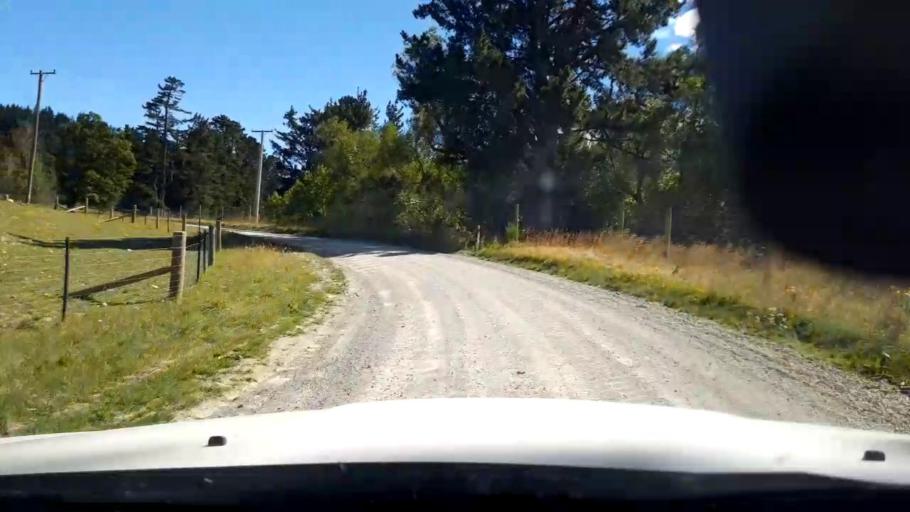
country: NZ
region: Canterbury
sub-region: Timaru District
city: Pleasant Point
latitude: -44.0300
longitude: 170.7437
